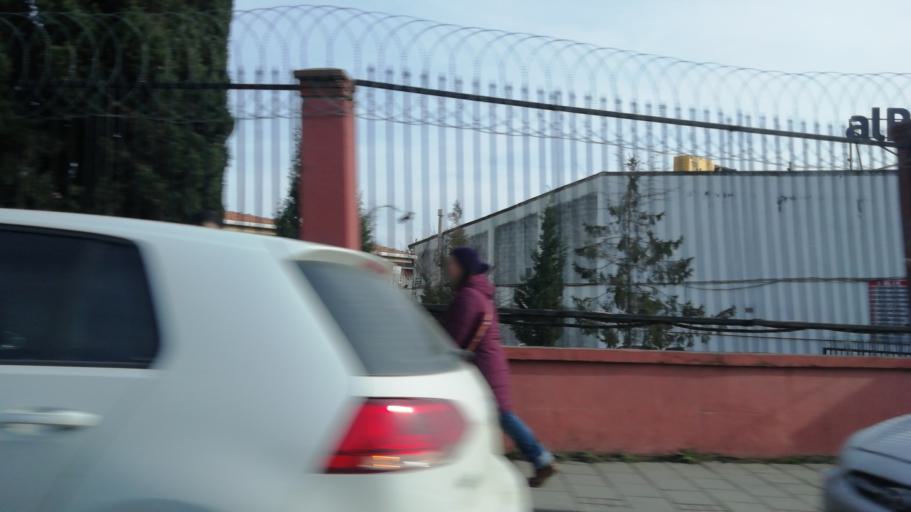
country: TR
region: Istanbul
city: Basaksehir
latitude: 41.0995
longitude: 28.7922
